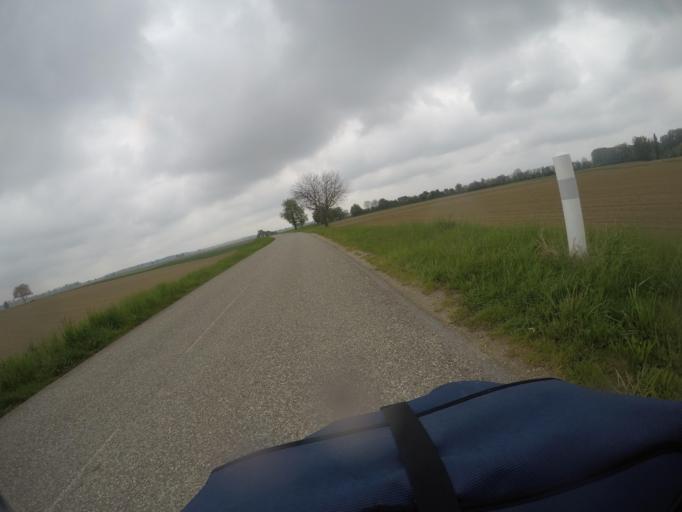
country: FR
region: Alsace
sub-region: Departement du Bas-Rhin
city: Roppenheim
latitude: 48.8229
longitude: 8.0650
